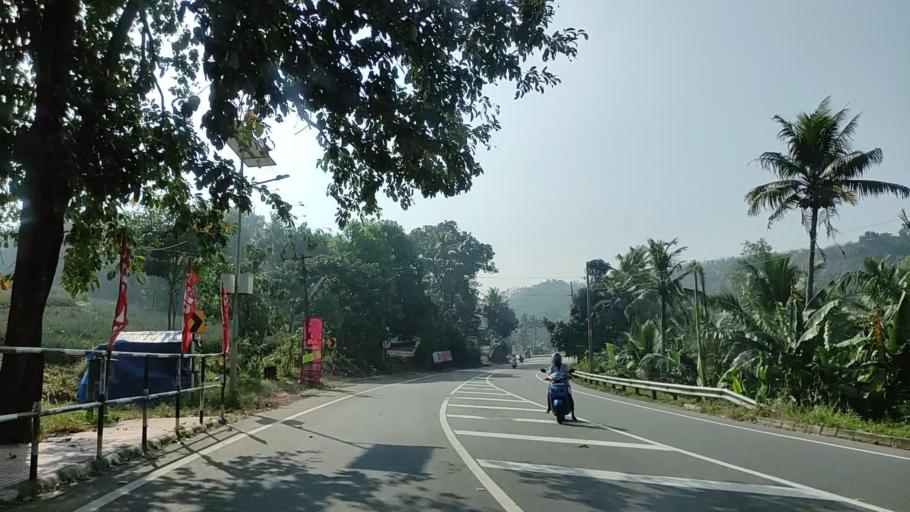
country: IN
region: Kerala
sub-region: Kollam
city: Punalur
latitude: 8.9625
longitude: 76.8373
